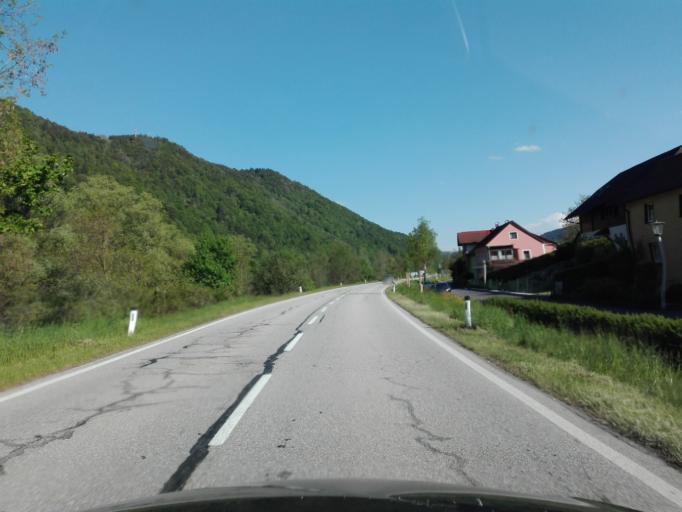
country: DE
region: Bavaria
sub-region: Lower Bavaria
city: Untergriesbach
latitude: 48.5105
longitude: 13.7280
